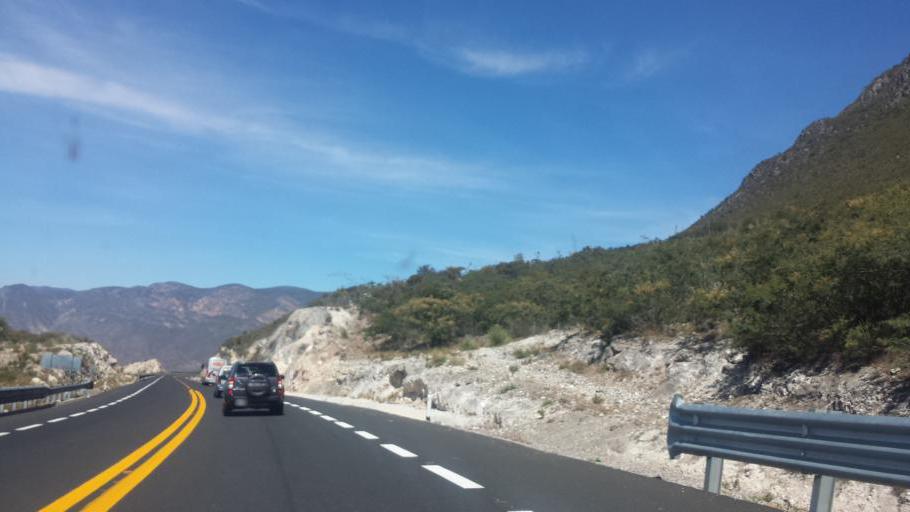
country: MX
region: Puebla
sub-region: San Jose Miahuatlan
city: San Pedro Tetitlan
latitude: 18.0718
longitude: -97.3521
